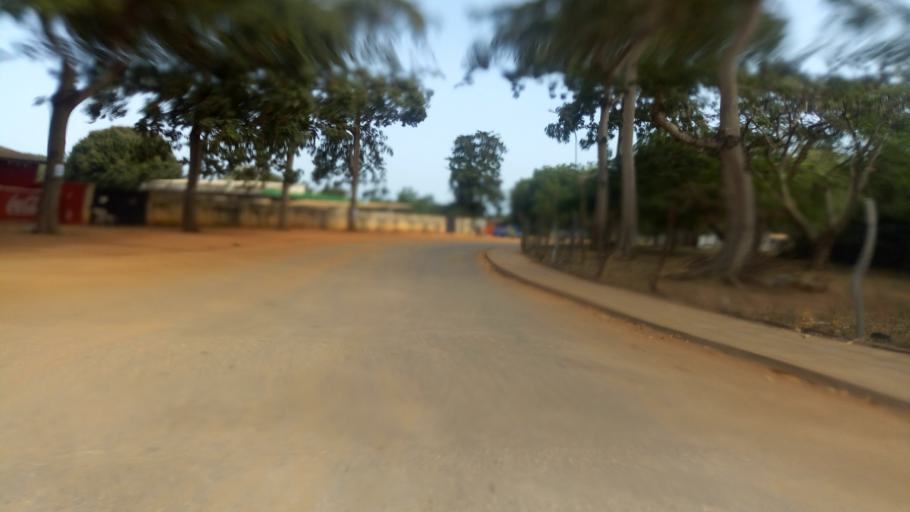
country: TG
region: Maritime
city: Lome
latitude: 6.1804
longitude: 1.2130
